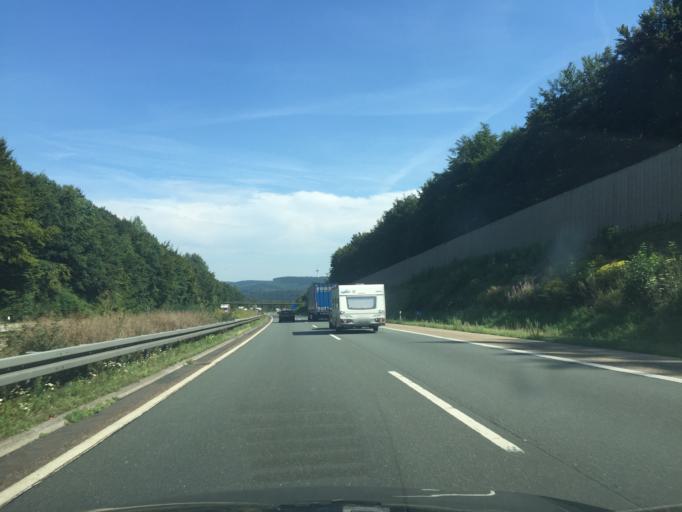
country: DE
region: North Rhine-Westphalia
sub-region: Regierungsbezirk Arnsberg
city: Siegen
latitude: 50.8674
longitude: 7.9705
